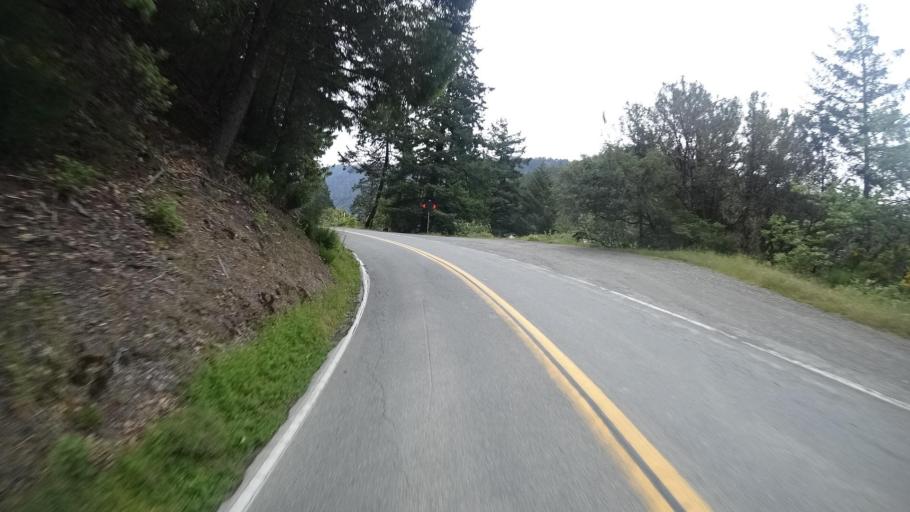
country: US
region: California
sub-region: Humboldt County
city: Willow Creek
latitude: 41.1865
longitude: -123.7056
